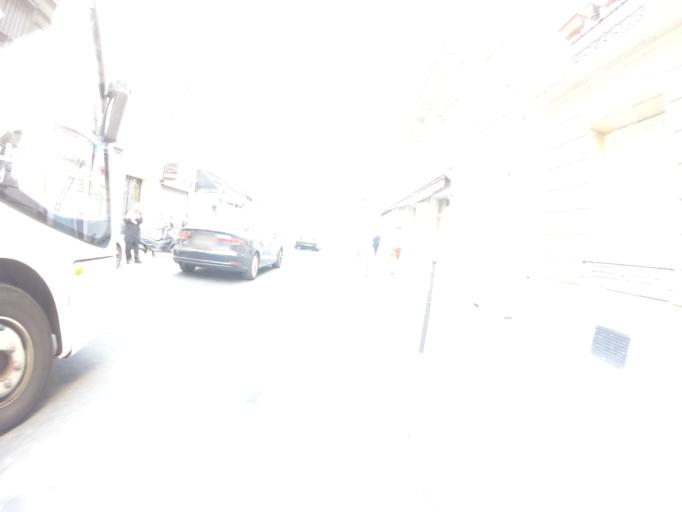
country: FR
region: Ile-de-France
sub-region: Departement des Hauts-de-Seine
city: Vanves
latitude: 48.8313
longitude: 2.2927
